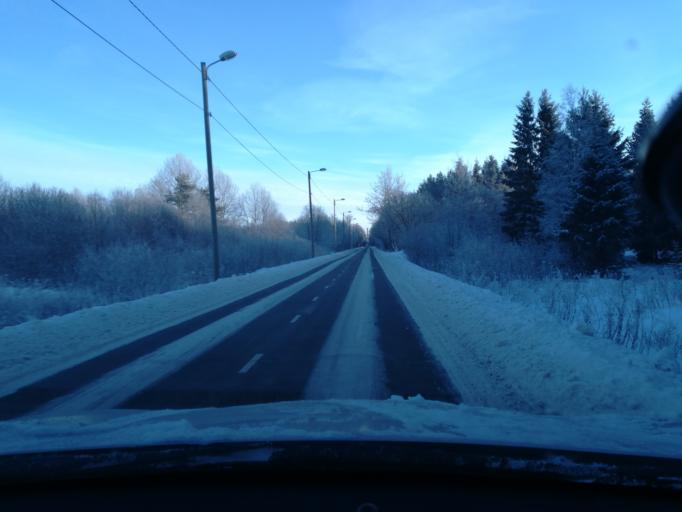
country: EE
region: Harju
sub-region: Saue vald
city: Laagri
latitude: 59.3918
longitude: 24.6083
